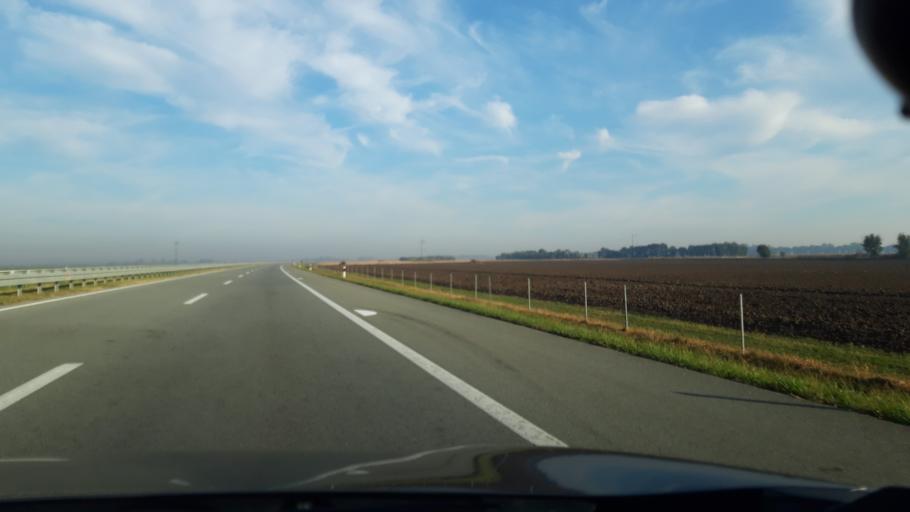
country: RS
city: Zmajevo
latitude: 45.5202
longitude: 19.7207
